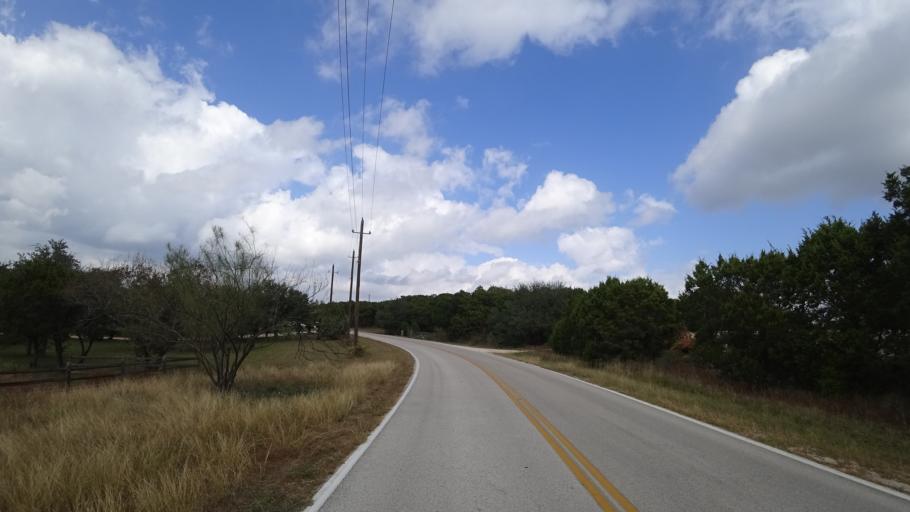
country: US
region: Texas
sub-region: Travis County
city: Barton Creek
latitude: 30.3055
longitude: -97.8786
